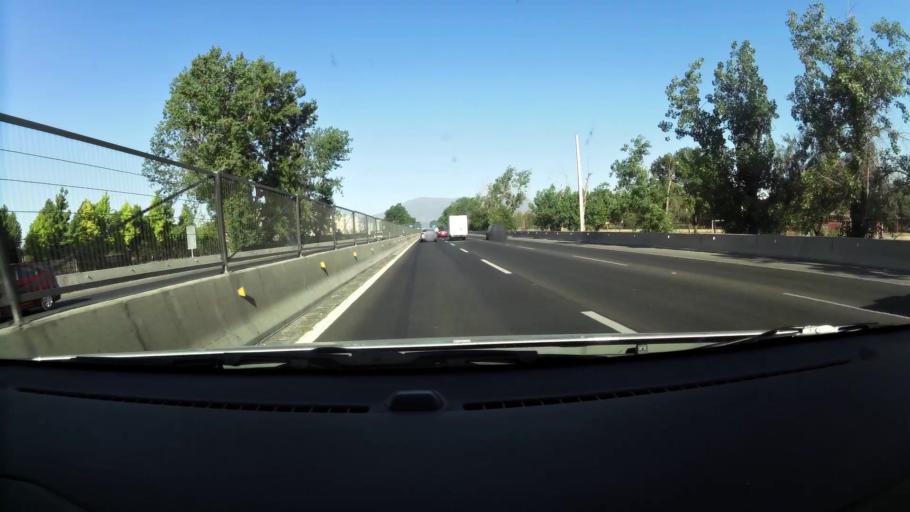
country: CL
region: Santiago Metropolitan
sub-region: Provincia de Santiago
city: Lo Prado
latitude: -33.4519
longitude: -70.7469
